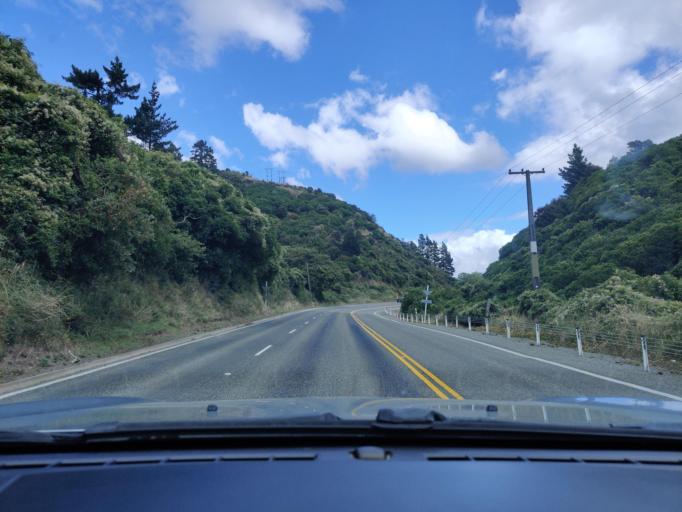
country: NZ
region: Marlborough
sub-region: Marlborough District
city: Picton
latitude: -41.3046
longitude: 173.9924
